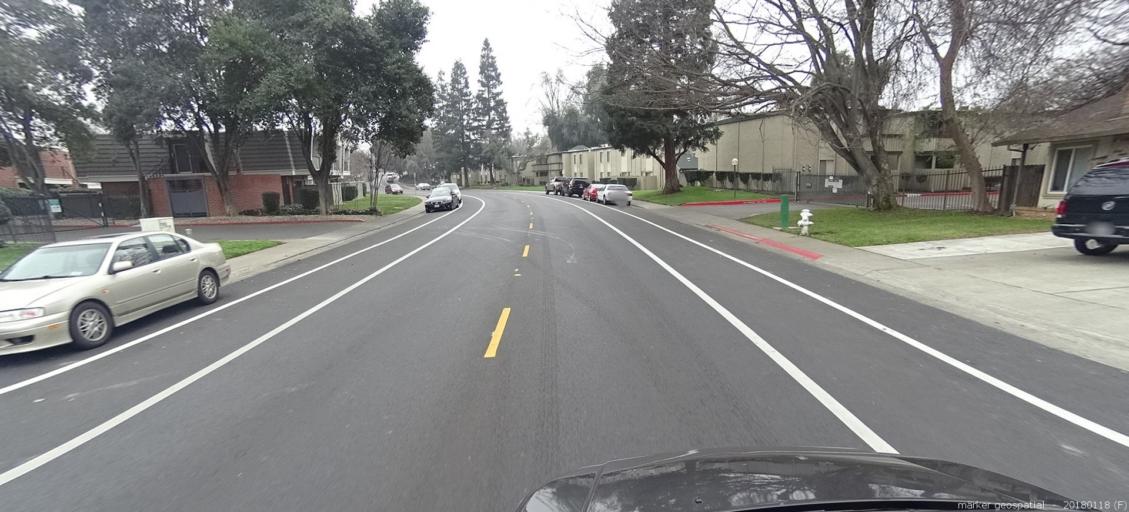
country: US
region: California
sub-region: Sacramento County
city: Rancho Cordova
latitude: 38.5861
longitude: -121.3152
